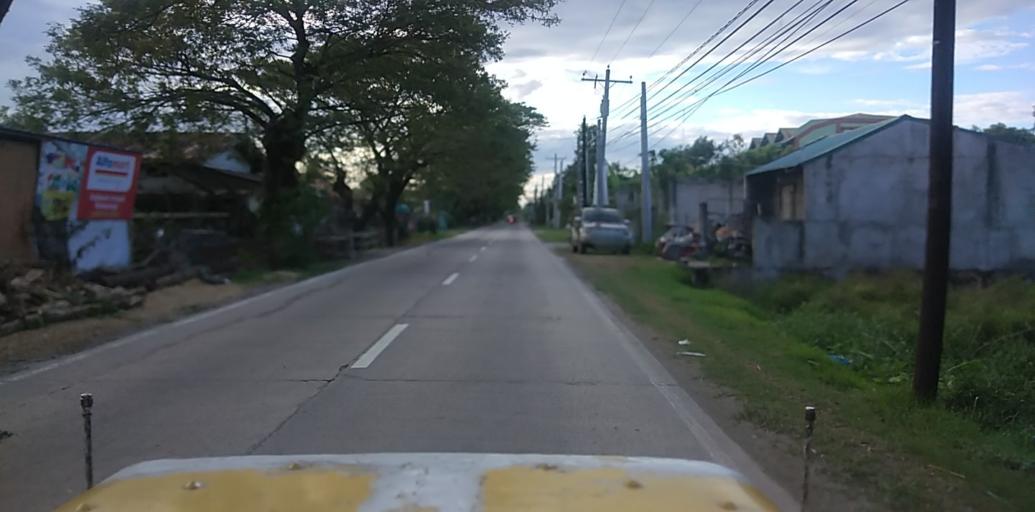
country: PH
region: Central Luzon
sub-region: Province of Pampanga
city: Arayat
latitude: 15.1522
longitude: 120.7385
